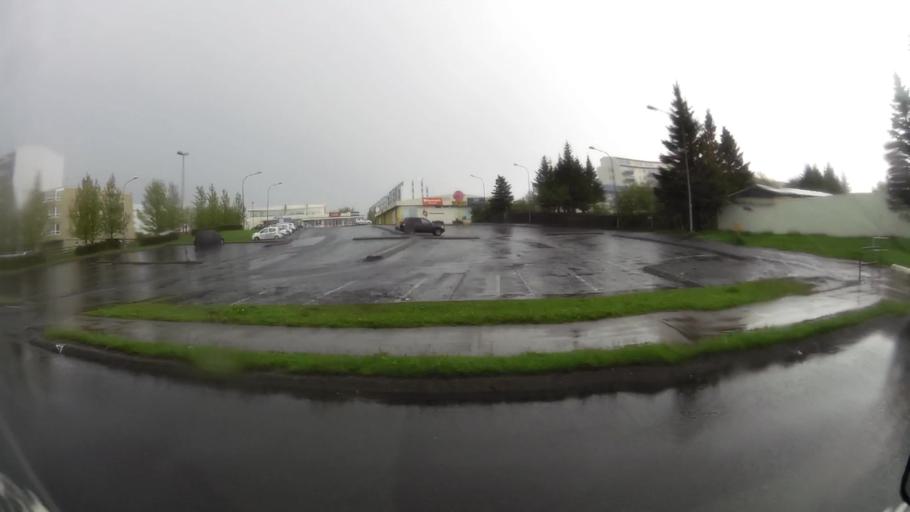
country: IS
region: Capital Region
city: Reykjavik
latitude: 64.1079
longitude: -21.8174
